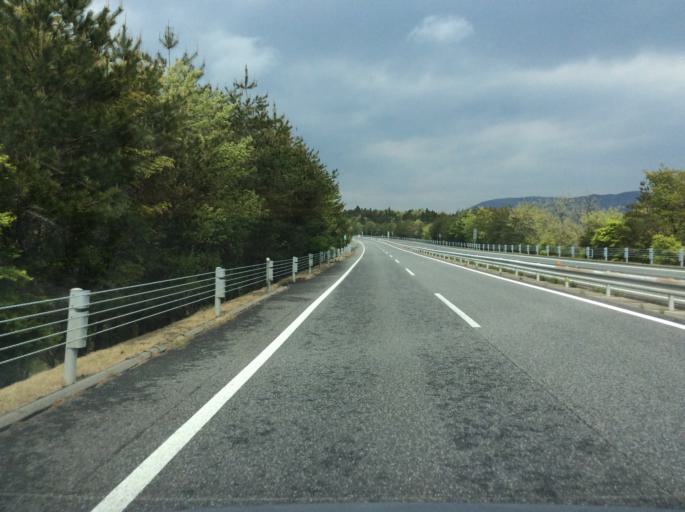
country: JP
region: Fukushima
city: Iwaki
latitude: 37.0486
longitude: 140.8059
